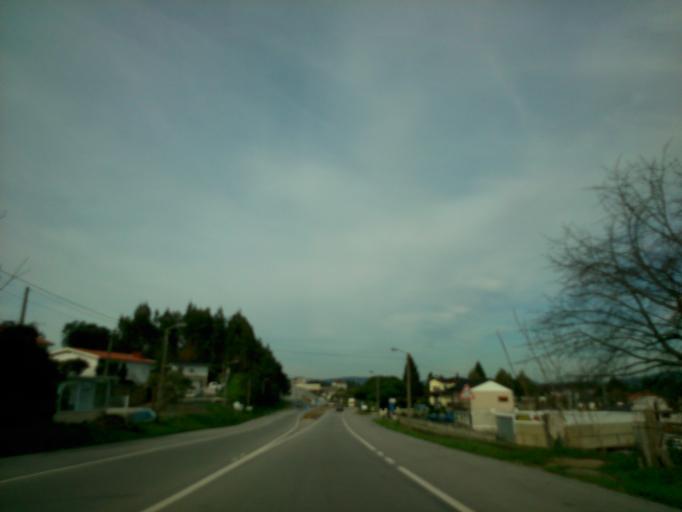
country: PT
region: Braga
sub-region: Barcelos
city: Barcelos
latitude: 41.5176
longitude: -8.5862
